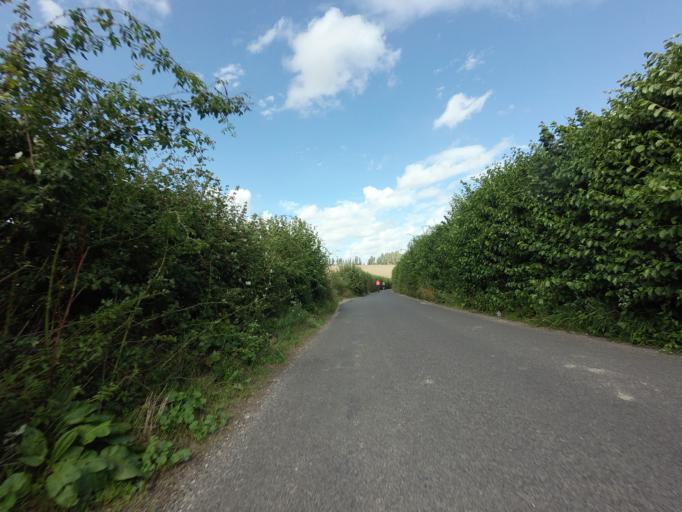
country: GB
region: England
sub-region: Kent
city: Shoreham
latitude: 51.3437
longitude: 0.1791
